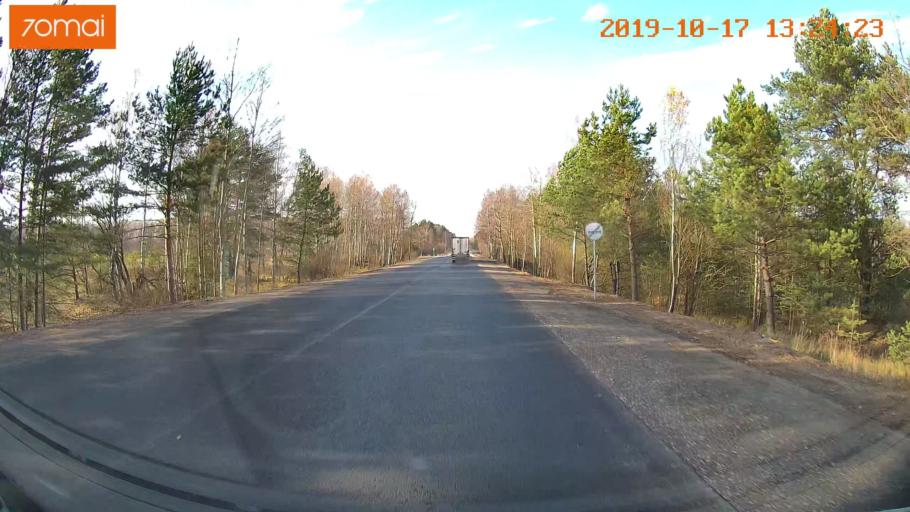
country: RU
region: Rjazan
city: Gus'-Zheleznyy
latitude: 55.0951
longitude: 40.9642
